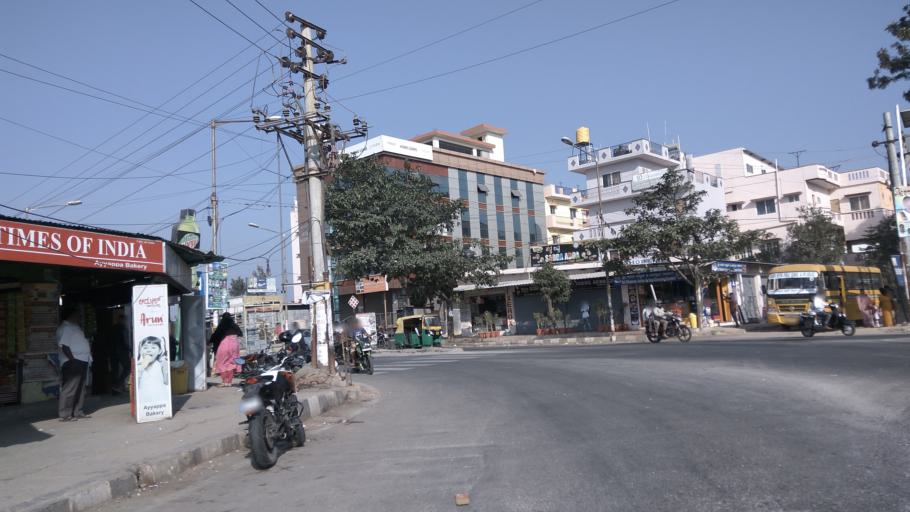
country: IN
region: Karnataka
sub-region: Bangalore Urban
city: Yelahanka
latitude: 13.1220
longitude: 77.6306
